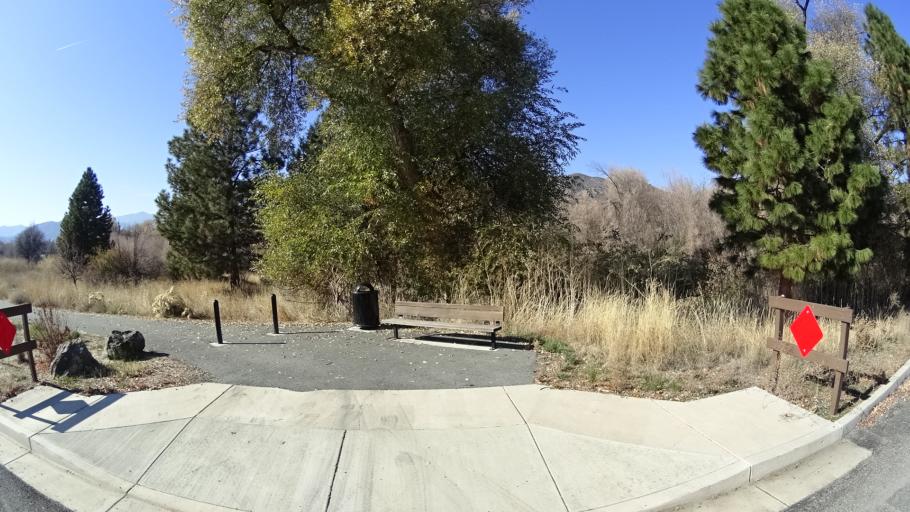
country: US
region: California
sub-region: Siskiyou County
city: Yreka
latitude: 41.7456
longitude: -122.6270
